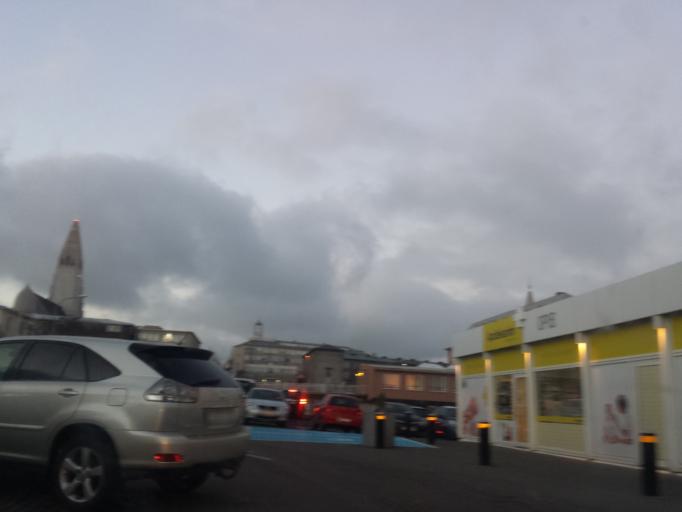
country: IS
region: Capital Region
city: Reykjavik
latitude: 64.1400
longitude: -21.9220
